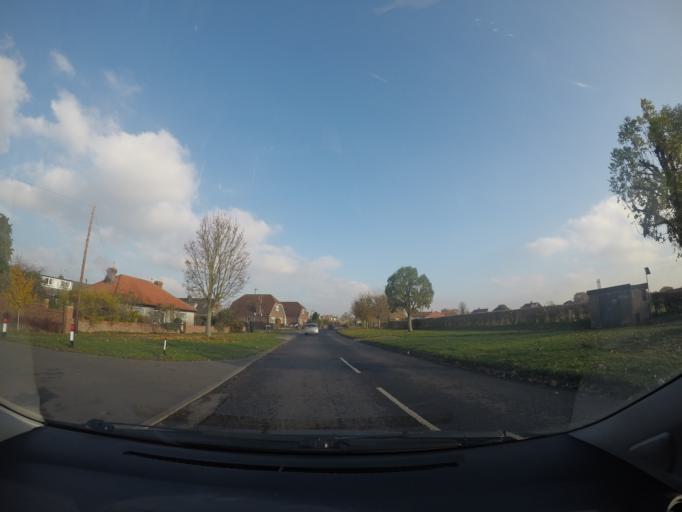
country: GB
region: England
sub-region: City of York
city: Huntington
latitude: 53.9983
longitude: -1.0574
